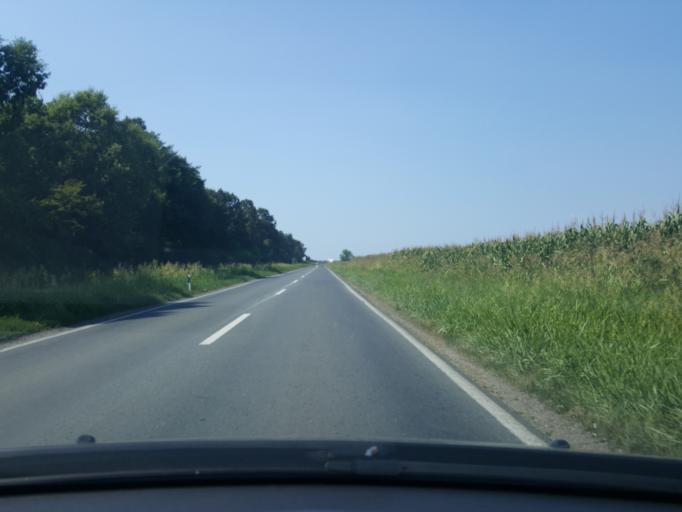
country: RS
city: Platicevo
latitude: 44.8394
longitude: 19.7701
